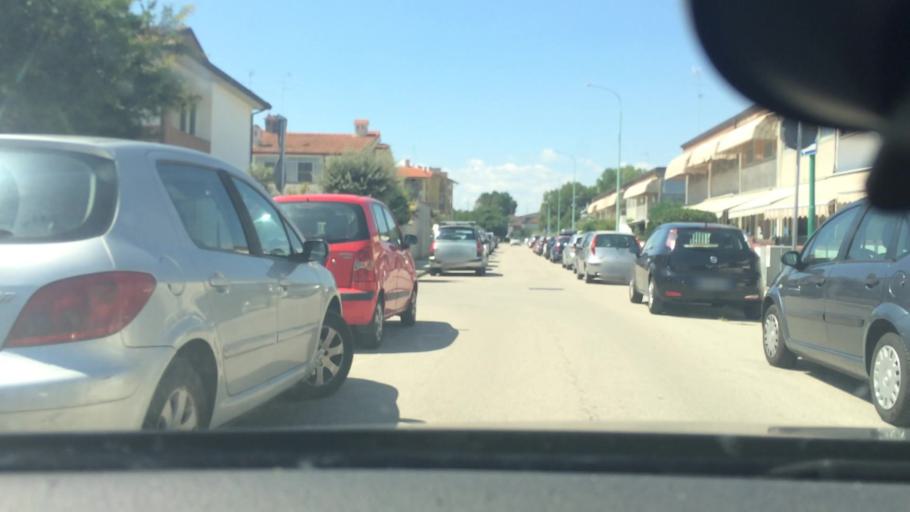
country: IT
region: Emilia-Romagna
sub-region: Provincia di Ferrara
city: Porto Garibaldi
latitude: 44.6839
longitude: 12.2400
